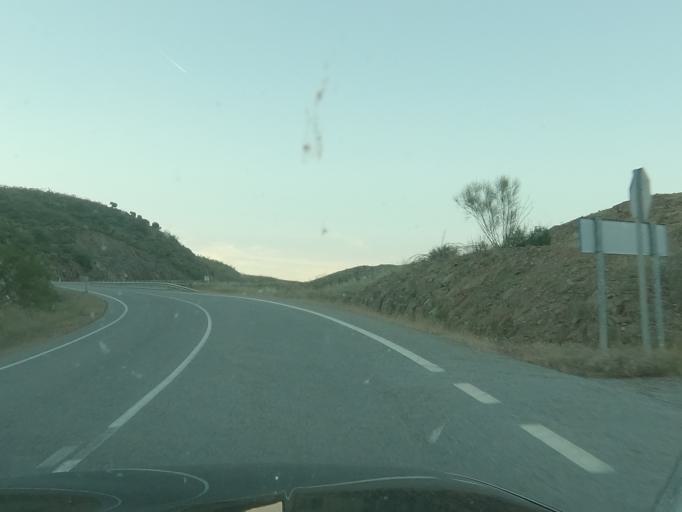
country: ES
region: Extremadura
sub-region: Provincia de Caceres
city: Salorino
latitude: 39.5811
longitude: -6.9970
